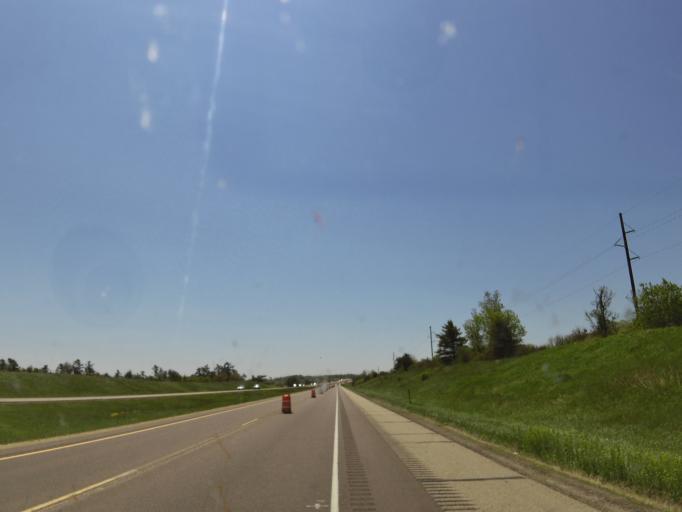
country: US
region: Wisconsin
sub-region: Monroe County
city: Tomah
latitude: 44.0649
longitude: -90.5196
